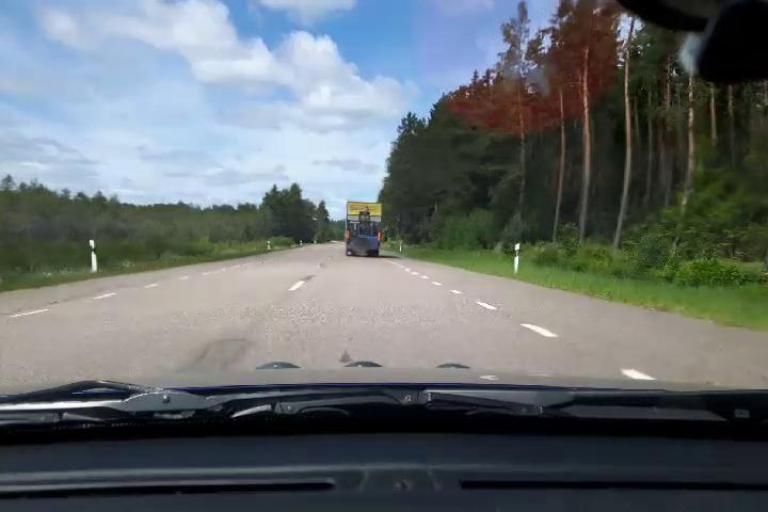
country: SE
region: Uppsala
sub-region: Osthammars Kommun
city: Bjorklinge
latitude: 60.1013
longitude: 17.5522
